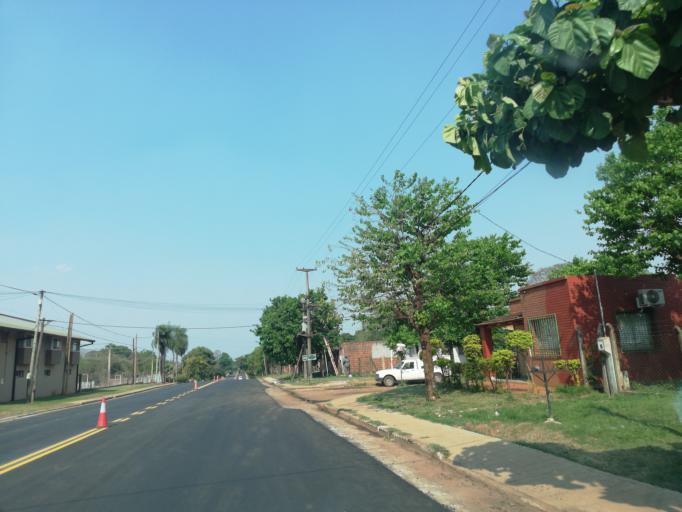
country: AR
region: Misiones
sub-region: Departamento de Capital
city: Posadas
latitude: -27.4077
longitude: -55.9095
